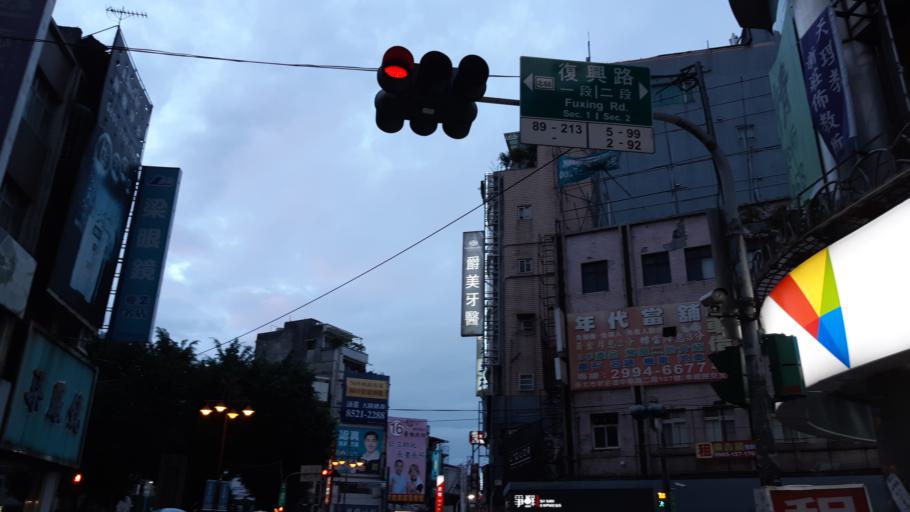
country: TW
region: Taipei
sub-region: Taipei
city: Banqiao
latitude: 25.0437
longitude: 121.4534
